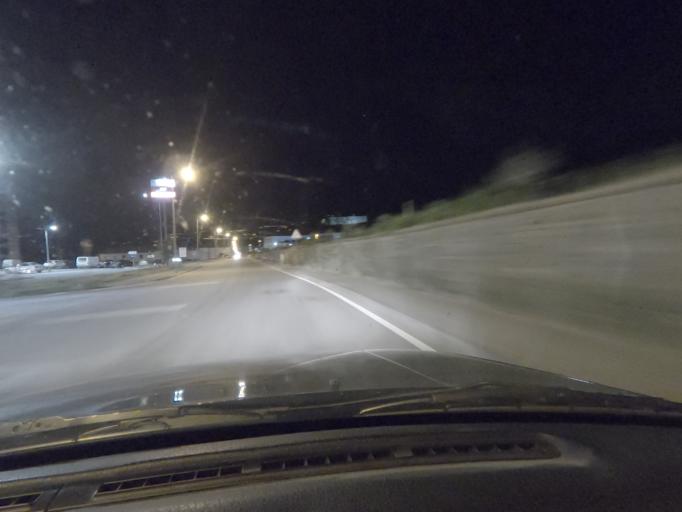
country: PT
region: Vila Real
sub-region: Peso da Regua
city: Godim
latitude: 41.1786
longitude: -7.7952
